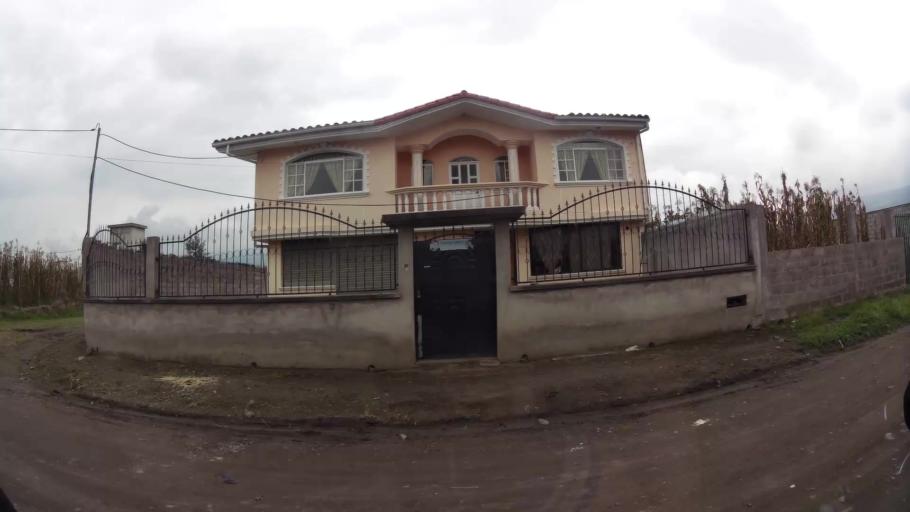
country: EC
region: Pichincha
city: Sangolqui
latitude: -0.3406
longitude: -78.4706
